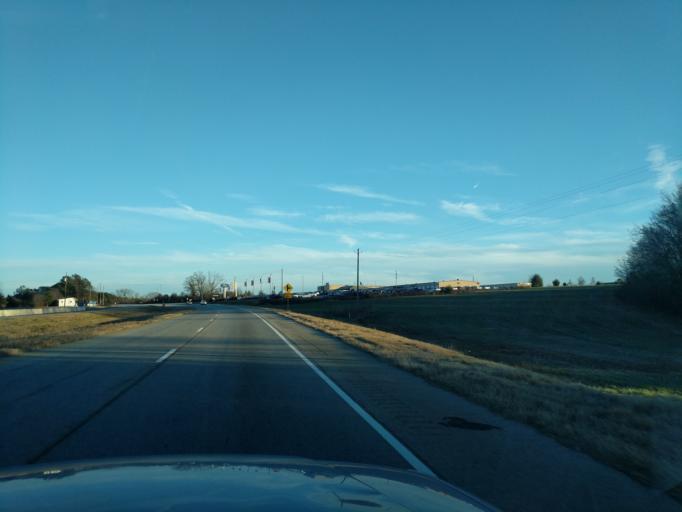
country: US
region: Georgia
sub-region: Franklin County
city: Lavonia
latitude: 34.4495
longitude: -83.1453
